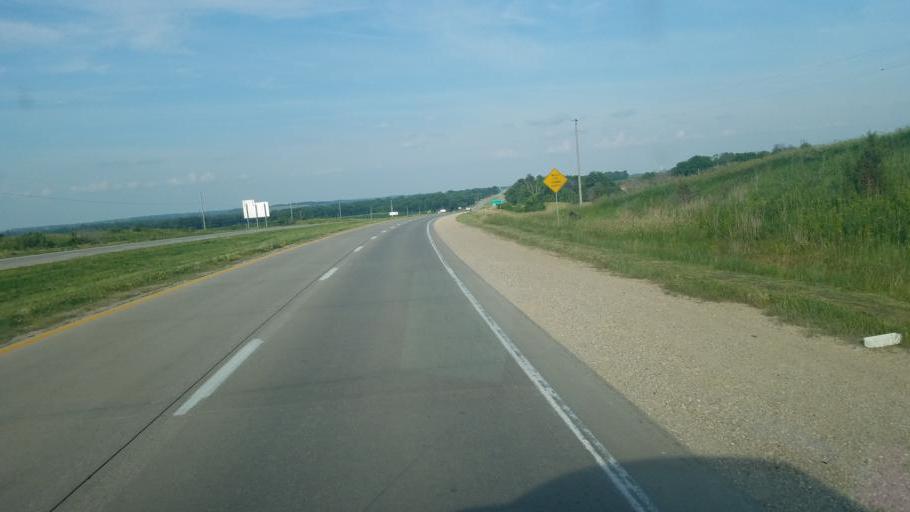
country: US
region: Iowa
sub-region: Marshall County
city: Marshalltown
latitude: 42.0066
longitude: -92.8675
